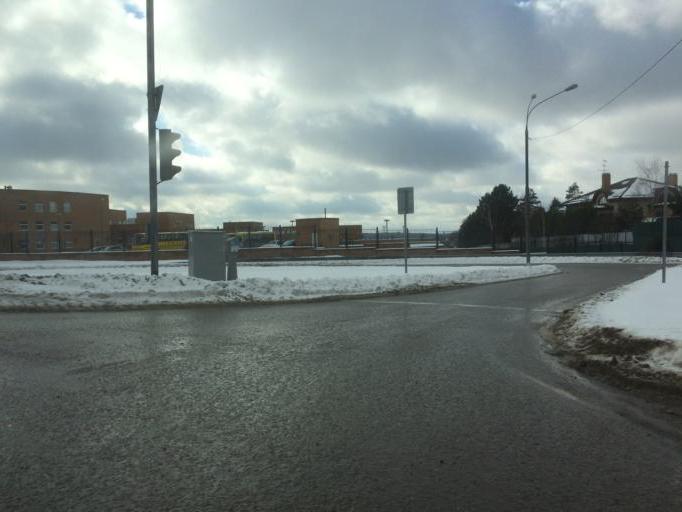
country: RU
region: Moskovskaya
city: Pavlovskaya Sloboda
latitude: 55.8029
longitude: 37.1271
